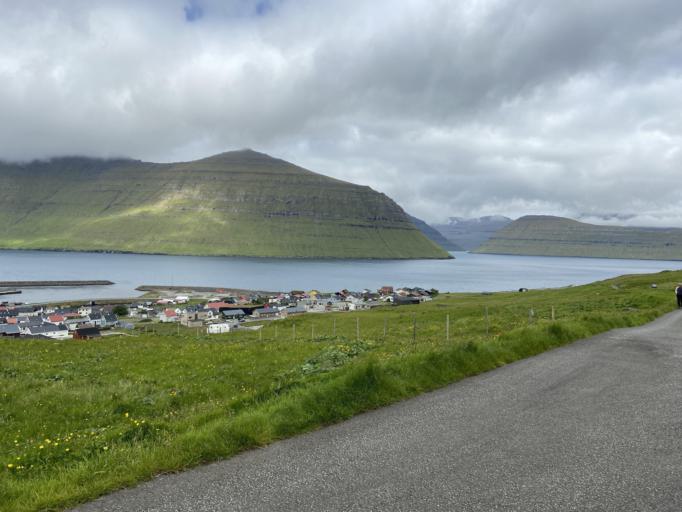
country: FO
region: Eysturoy
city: Eystur
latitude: 62.2052
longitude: -6.7051
